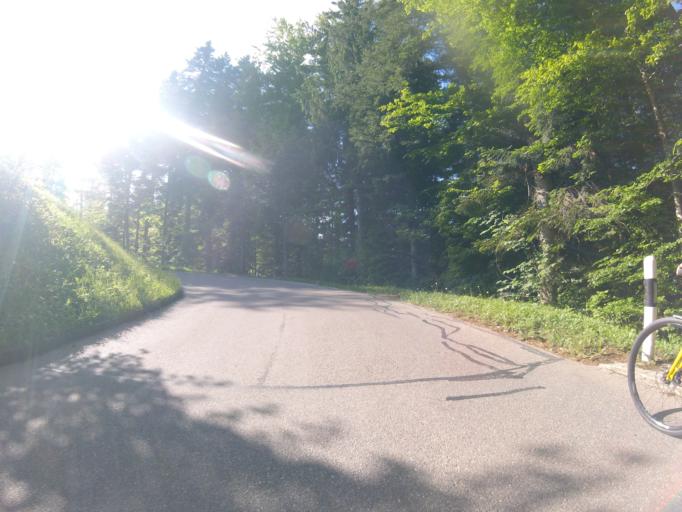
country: CH
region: Saint Gallen
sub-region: Wahlkreis Toggenburg
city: Mogelsberg
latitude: 47.3638
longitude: 9.1451
